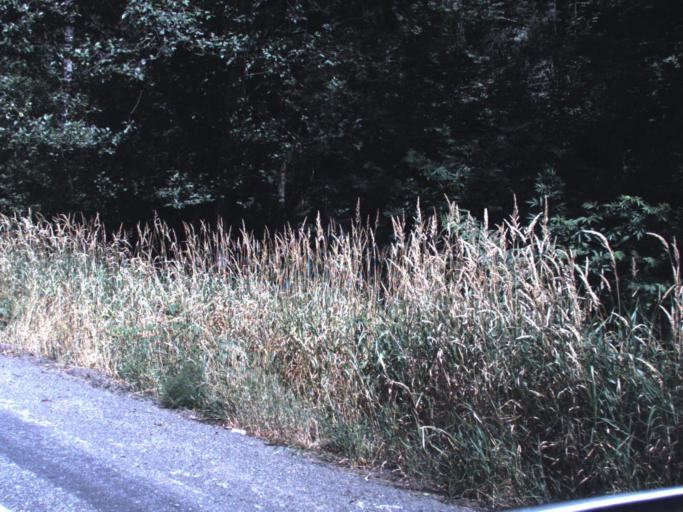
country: US
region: Washington
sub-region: King County
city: Enumclaw
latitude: 47.1948
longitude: -121.9392
